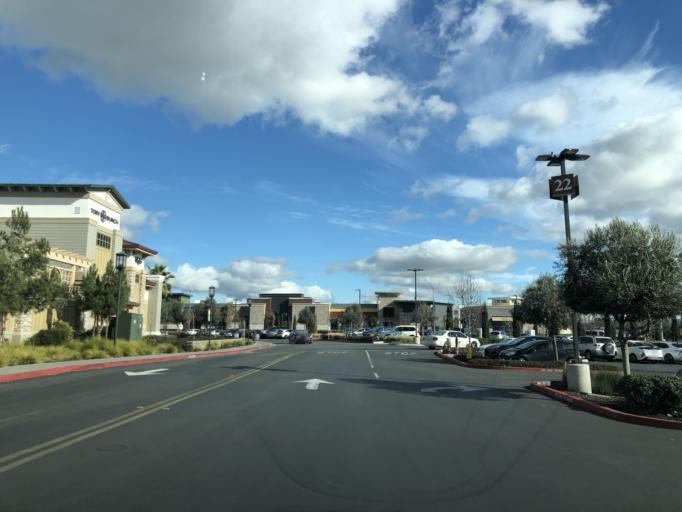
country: US
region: California
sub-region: Alameda County
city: Pleasanton
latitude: 37.6980
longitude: -121.8416
